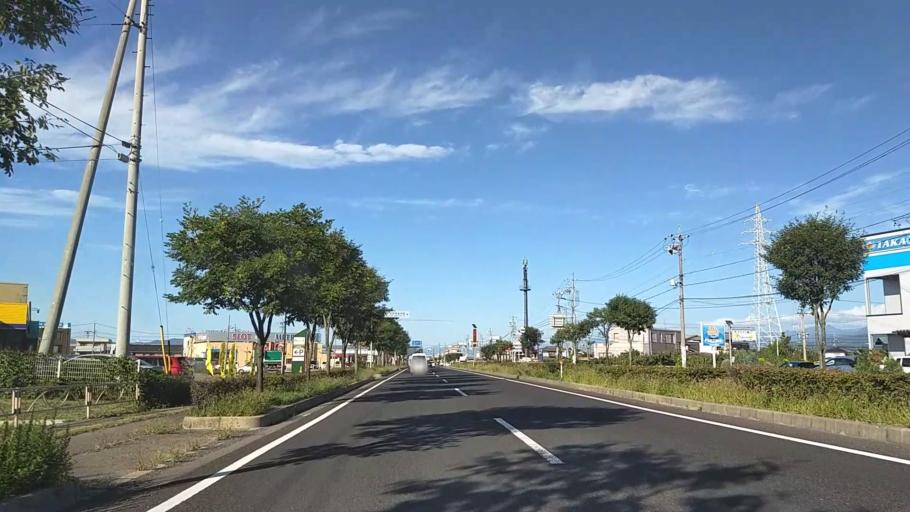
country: JP
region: Nagano
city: Nagano-shi
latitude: 36.5733
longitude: 138.1541
